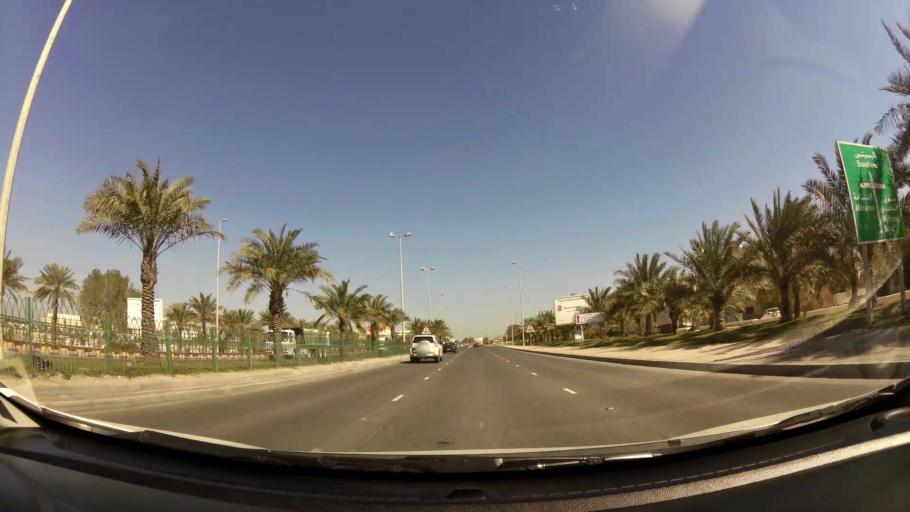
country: BH
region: Muharraq
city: Al Muharraq
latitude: 26.2578
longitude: 50.6034
